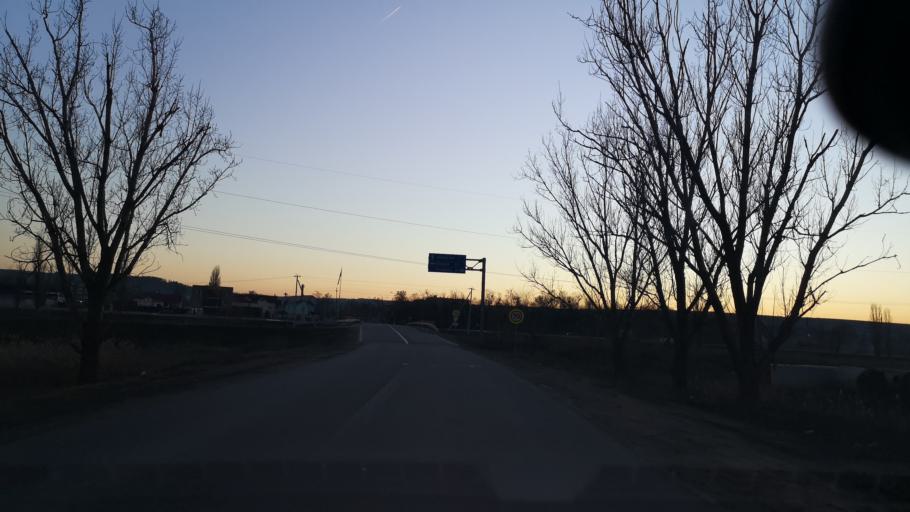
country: MD
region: Anenii Noi
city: Anenii Noi
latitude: 46.8872
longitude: 29.2363
